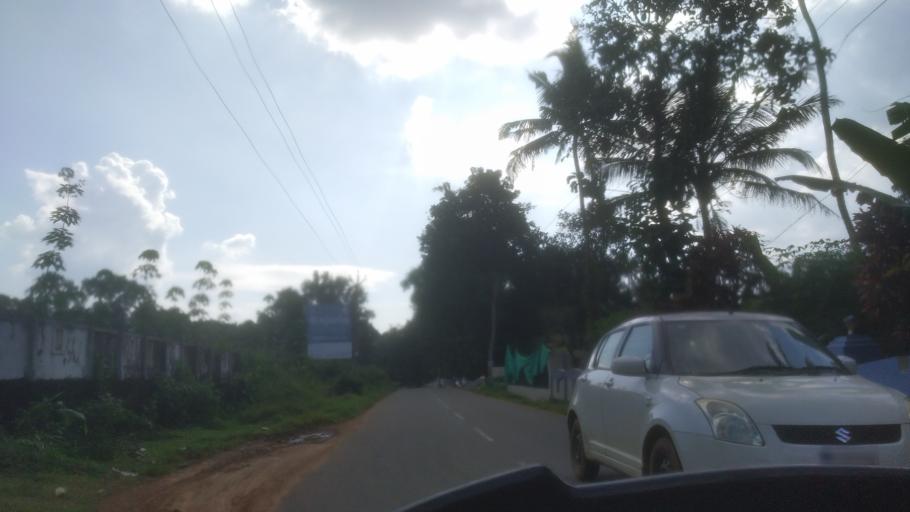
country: IN
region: Kerala
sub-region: Ernakulam
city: Kotamangalam
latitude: 10.0029
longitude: 76.6522
